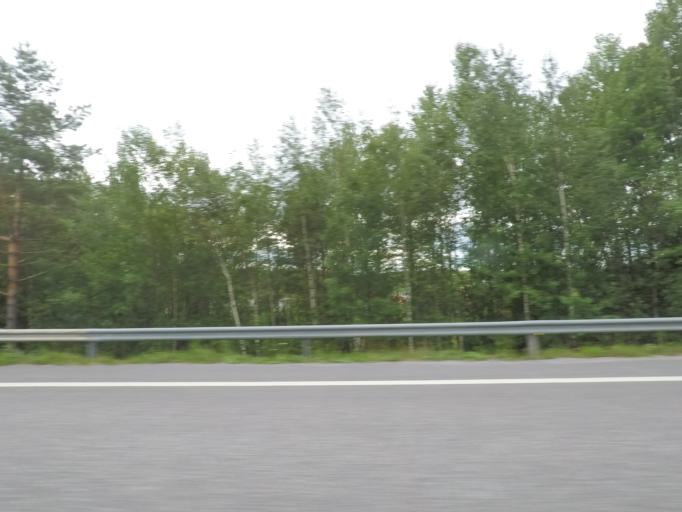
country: FI
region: Uusimaa
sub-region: Helsinki
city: Kerava
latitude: 60.3665
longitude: 25.1169
